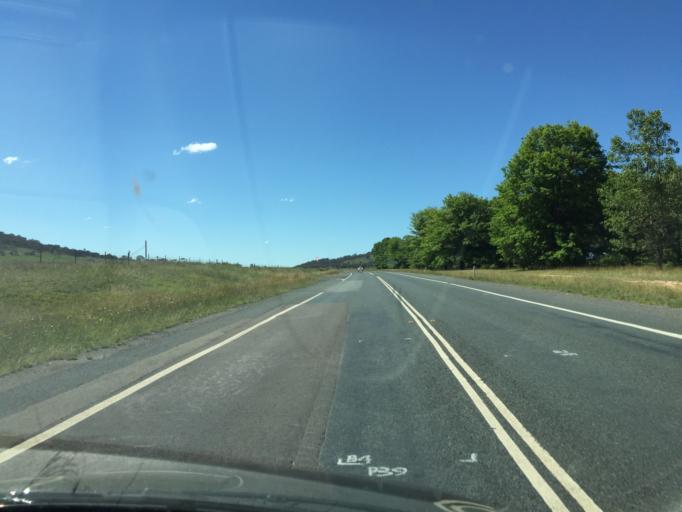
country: AU
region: Australian Capital Territory
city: Macarthur
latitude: -35.4910
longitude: 149.1503
